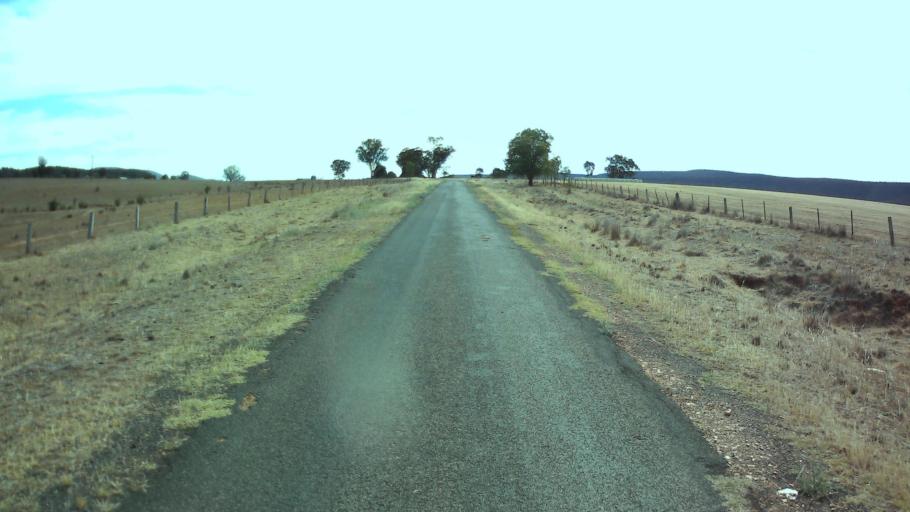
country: AU
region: New South Wales
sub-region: Weddin
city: Grenfell
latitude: -33.8340
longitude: 148.2720
